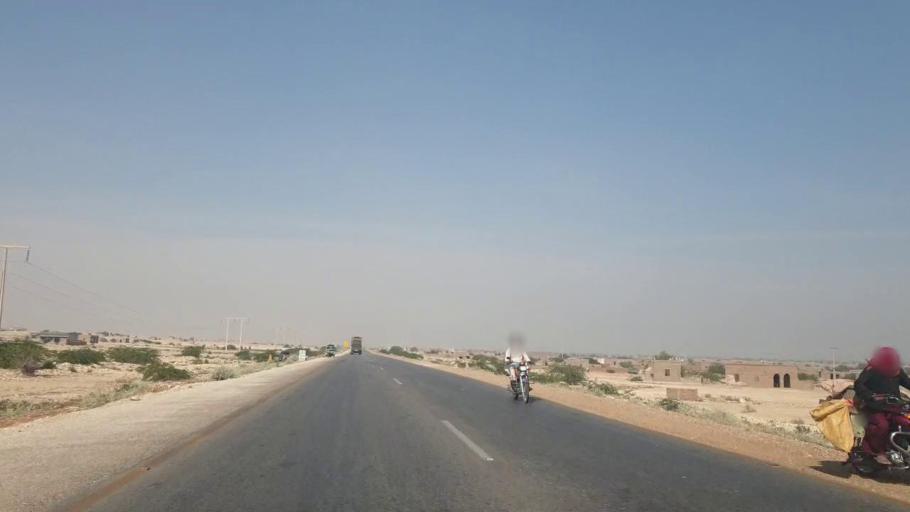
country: PK
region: Sindh
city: Hala
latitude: 25.7747
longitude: 68.2852
